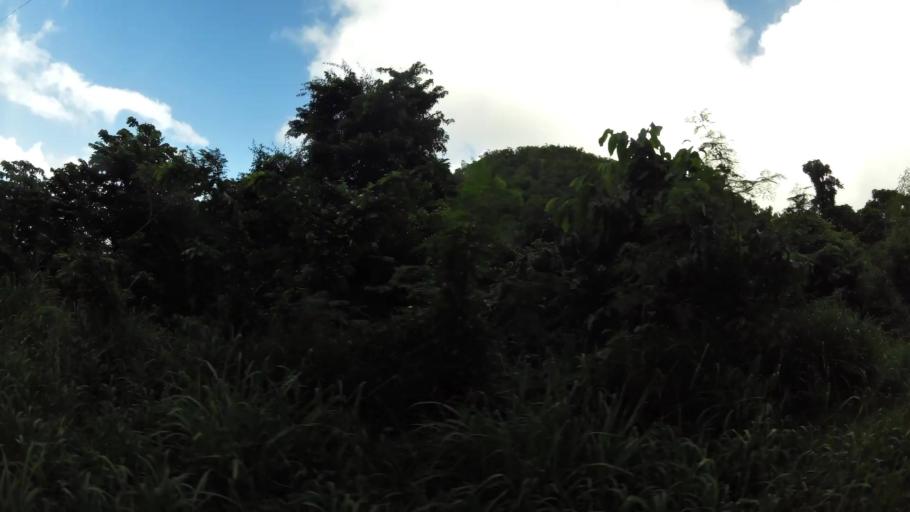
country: MQ
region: Martinique
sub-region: Martinique
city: Les Trois-Ilets
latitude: 14.5109
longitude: -61.0761
